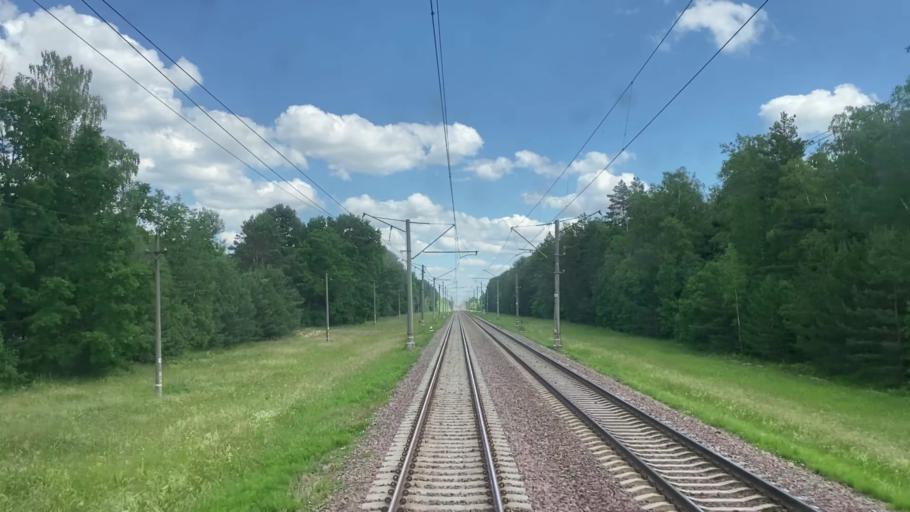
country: BY
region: Brest
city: Nyakhachava
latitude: 52.6609
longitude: 25.2410
